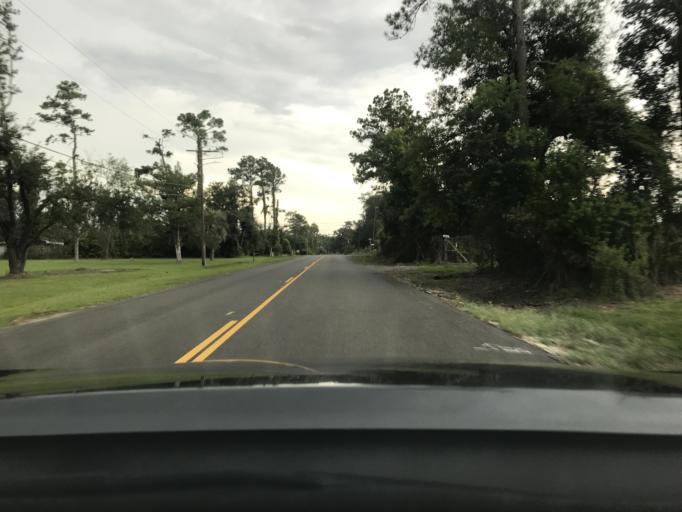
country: US
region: Louisiana
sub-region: Calcasieu Parish
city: Westlake
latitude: 30.2744
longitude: -93.2396
